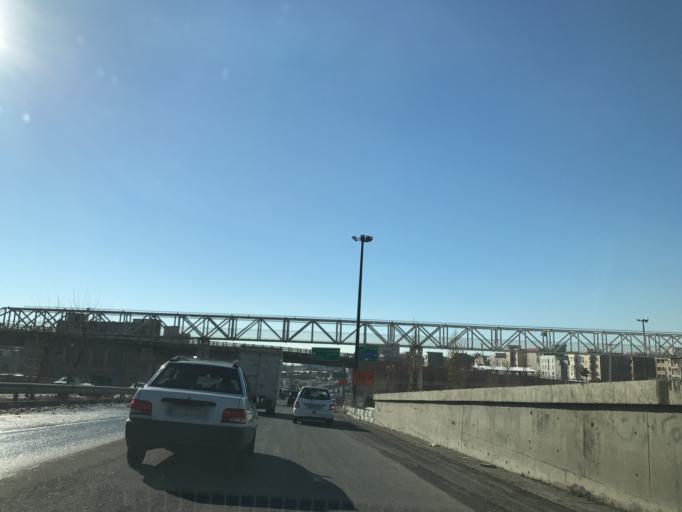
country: IR
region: Tehran
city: Tehran
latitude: 35.6364
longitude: 51.3557
